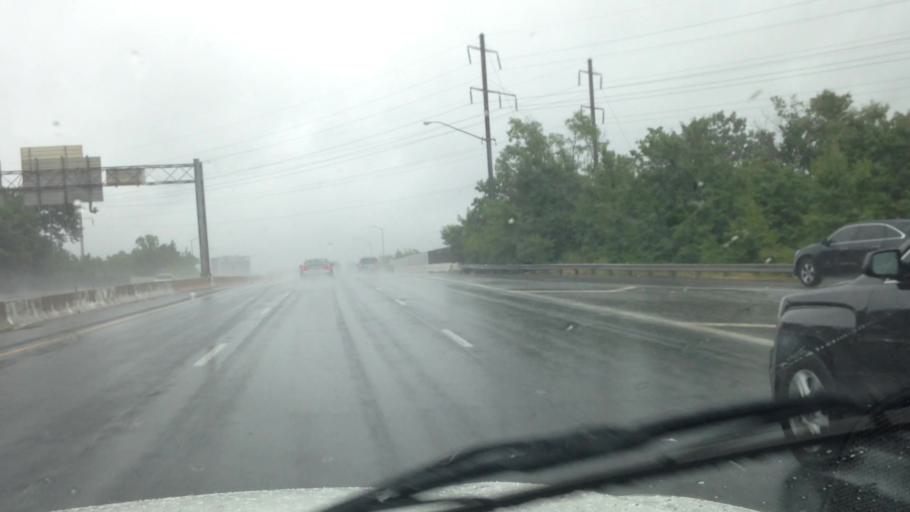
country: US
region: Maryland
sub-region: Prince George's County
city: Landover Hills
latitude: 38.9437
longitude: -76.8787
